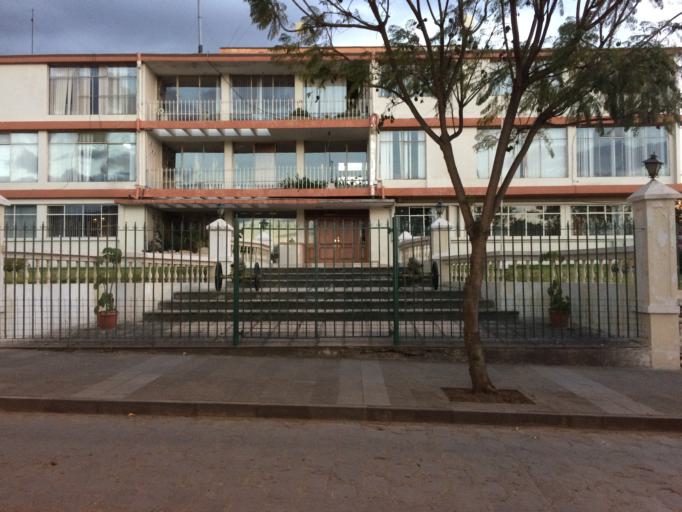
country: EC
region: Azuay
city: Cuenca
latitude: -2.8912
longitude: -79.0012
